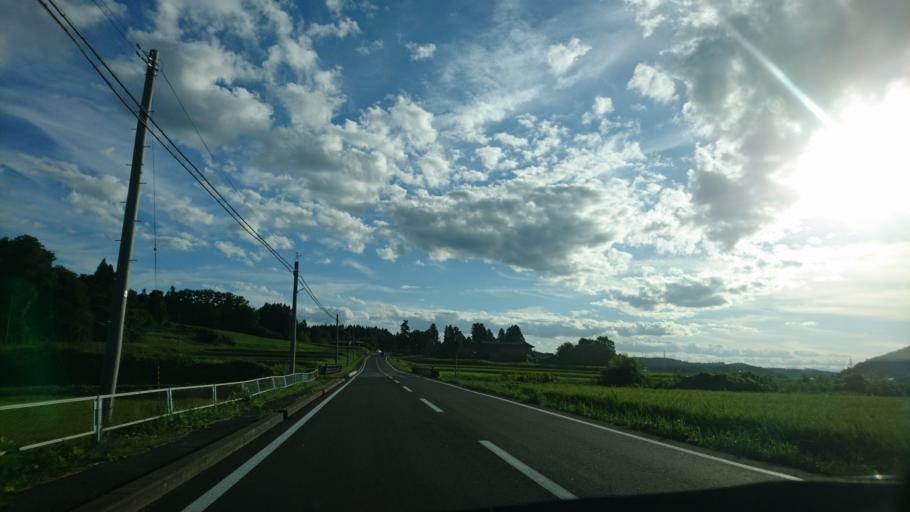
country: JP
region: Iwate
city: Ichinoseki
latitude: 38.8430
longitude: 141.1532
